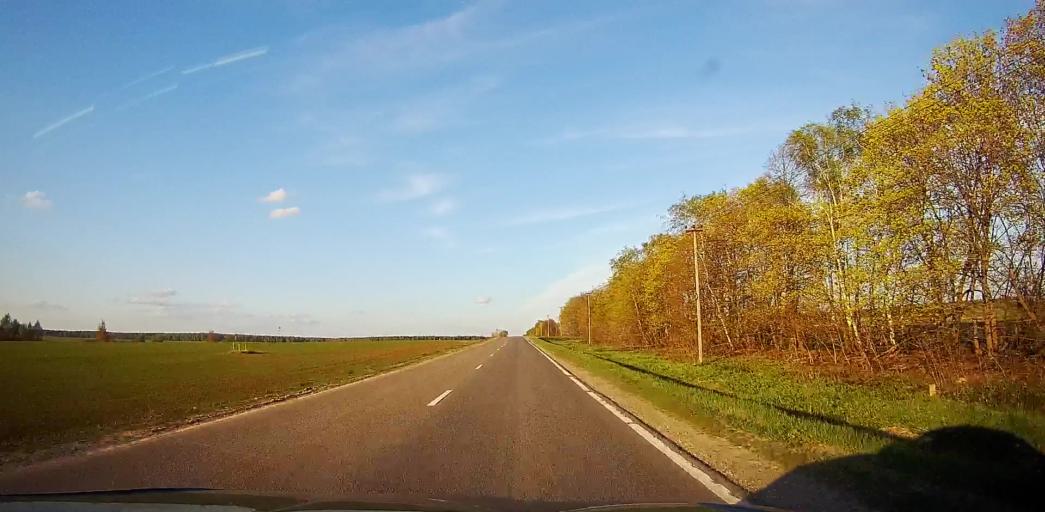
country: RU
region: Moskovskaya
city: Bronnitsy
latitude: 55.2844
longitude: 38.1791
